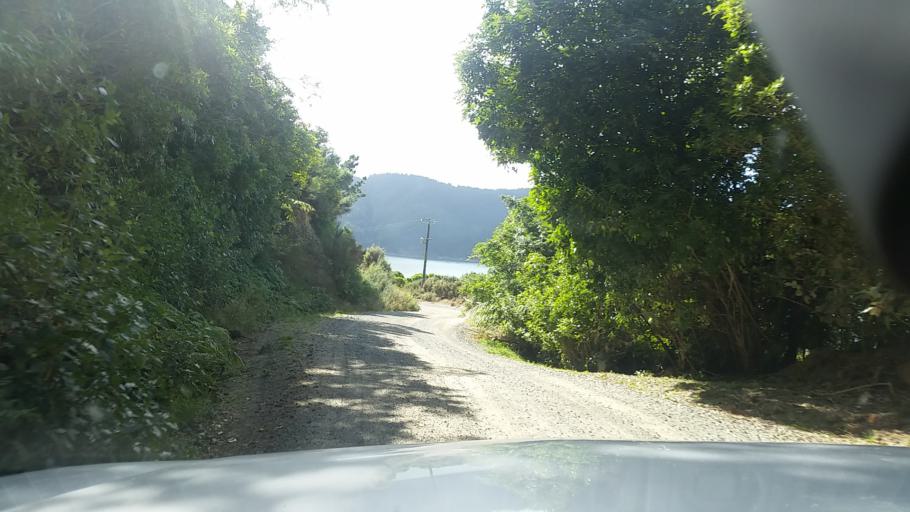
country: NZ
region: Marlborough
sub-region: Marlborough District
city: Picton
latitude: -41.2893
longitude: 174.1299
